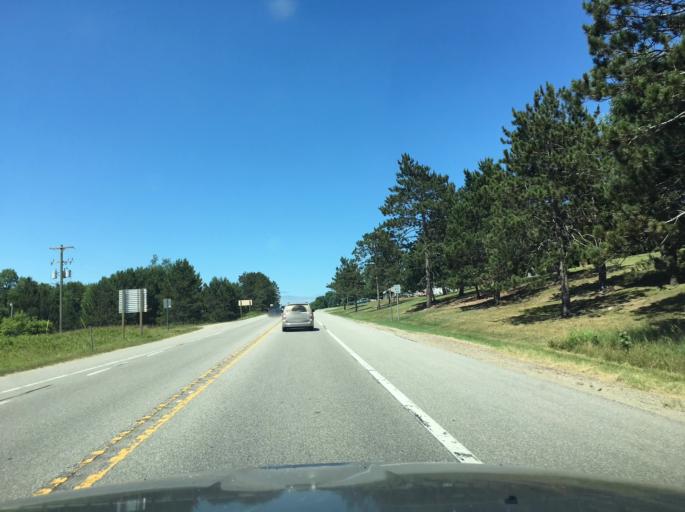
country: US
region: Michigan
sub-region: Osceola County
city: Reed City
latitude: 43.8875
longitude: -85.5366
